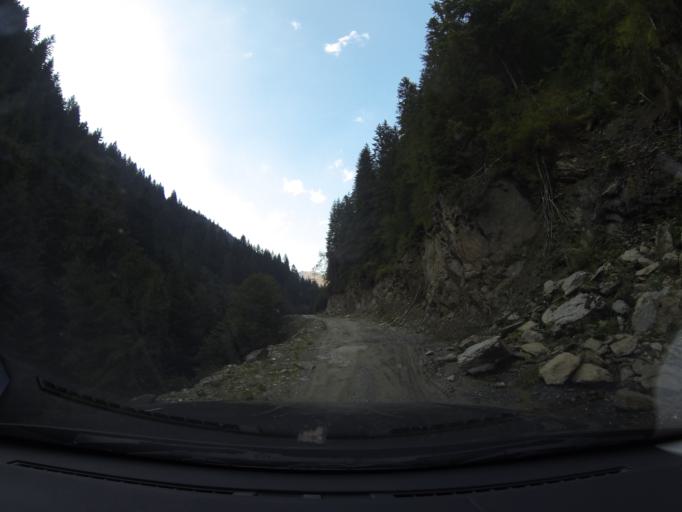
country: RO
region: Brasov
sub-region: Oras Victoria
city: Victoria
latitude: 45.5366
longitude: 24.6777
